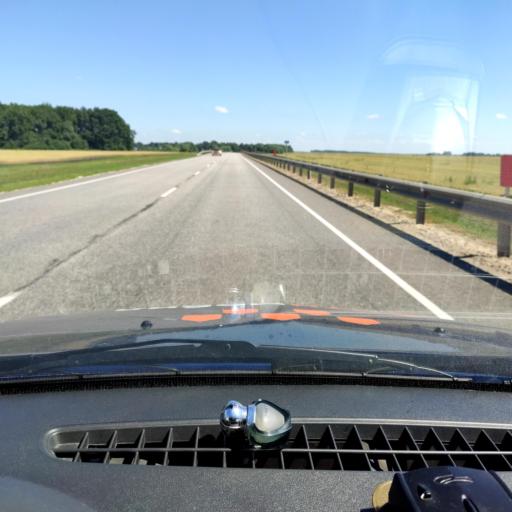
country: RU
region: Orjol
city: Pokrovskoye
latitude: 52.6245
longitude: 36.7198
